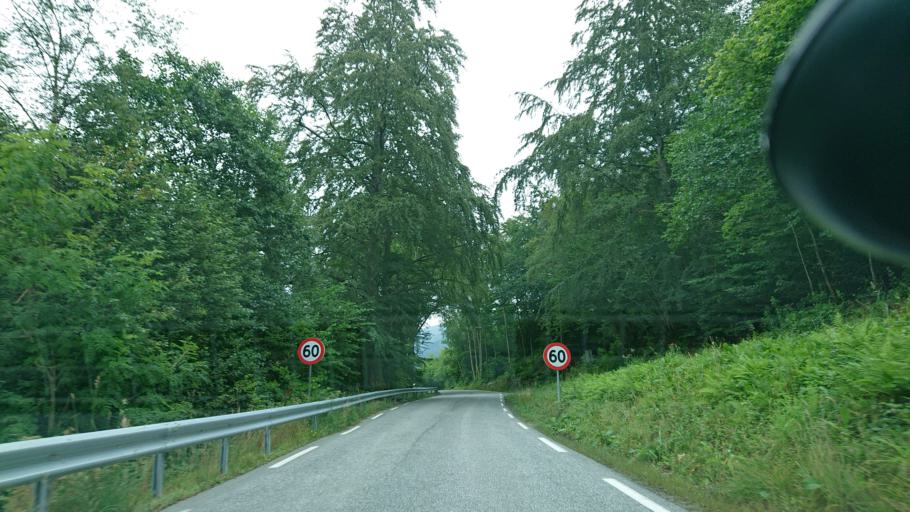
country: NO
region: Rogaland
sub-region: Hjelmeland
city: Hjelmelandsvagen
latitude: 59.2356
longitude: 6.1827
